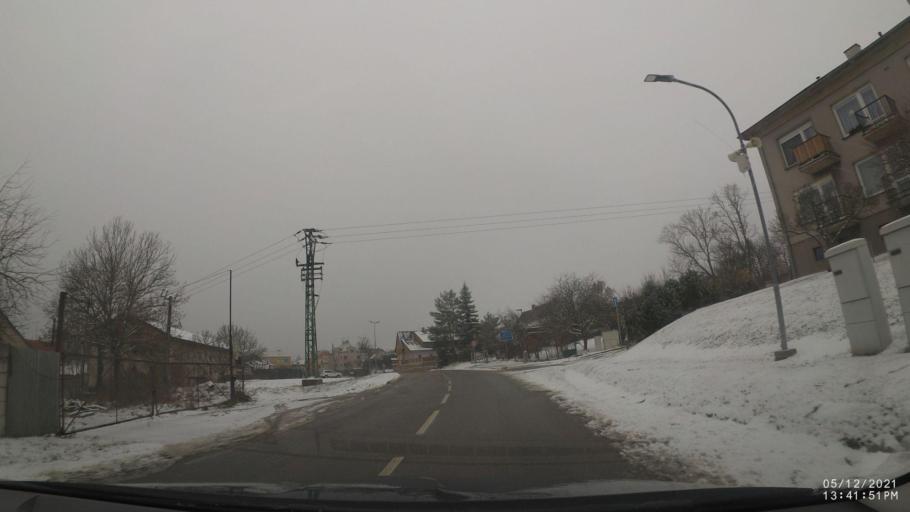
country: CZ
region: Kralovehradecky
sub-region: Okres Nachod
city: Police nad Metuji
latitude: 50.5339
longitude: 16.2400
